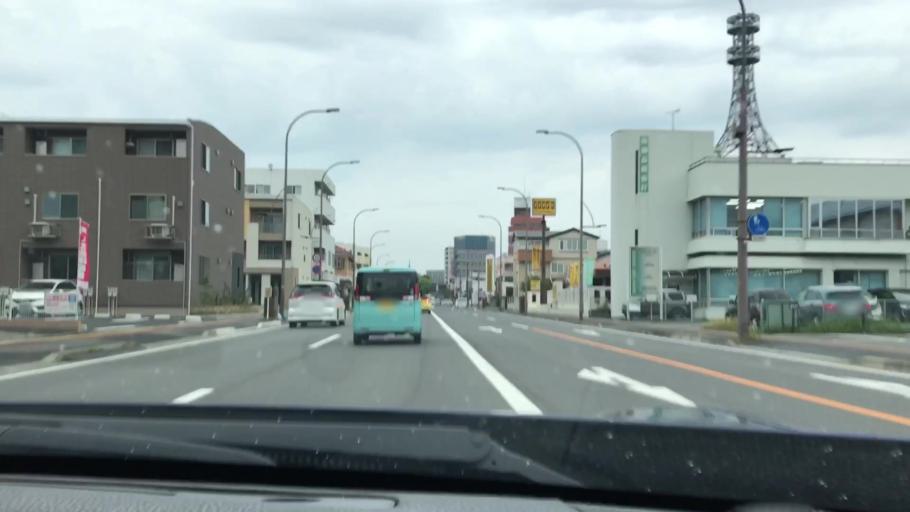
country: JP
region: Gunma
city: Maebashi-shi
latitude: 36.3791
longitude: 139.0694
